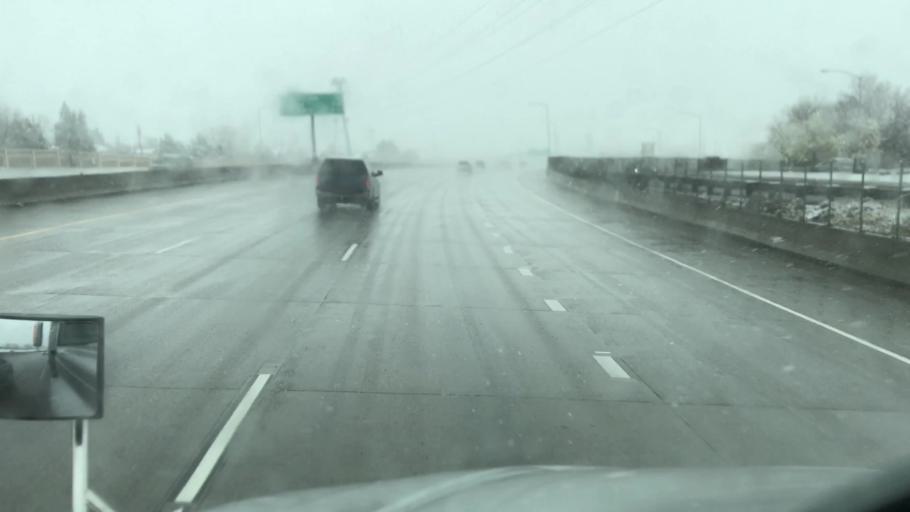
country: US
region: Colorado
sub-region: Adams County
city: Aurora
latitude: 39.7045
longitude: -104.8285
